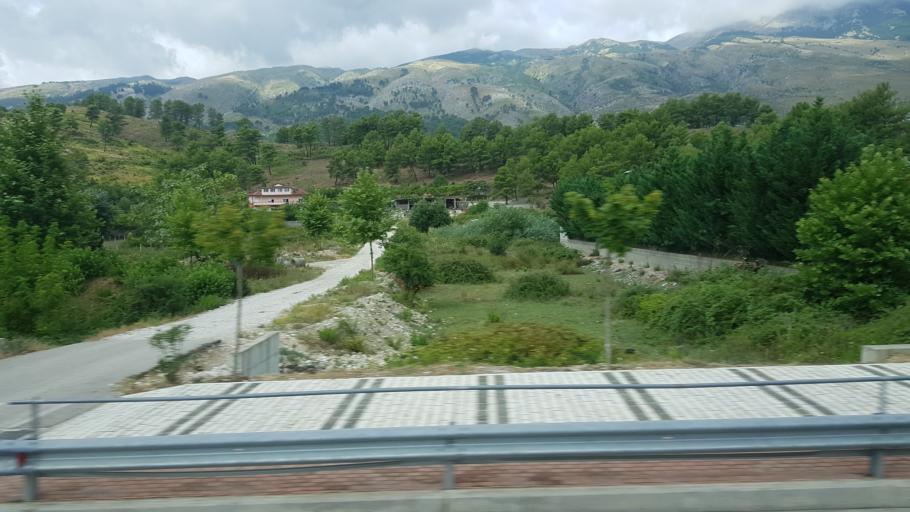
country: AL
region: Gjirokaster
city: Gjirokaster
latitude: 40.0992
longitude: 20.1299
